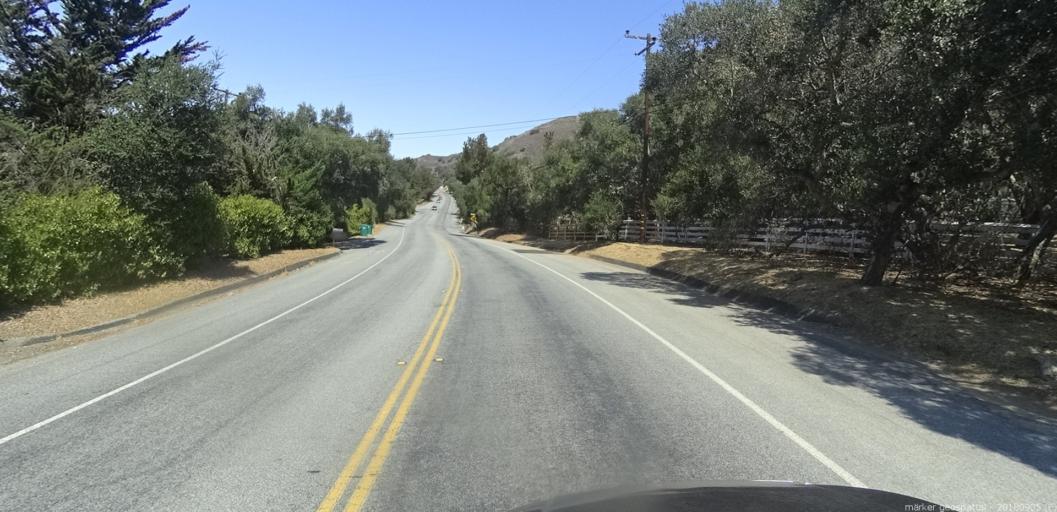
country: US
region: California
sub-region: Monterey County
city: Carmel Valley Village
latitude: 36.5056
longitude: -121.7523
